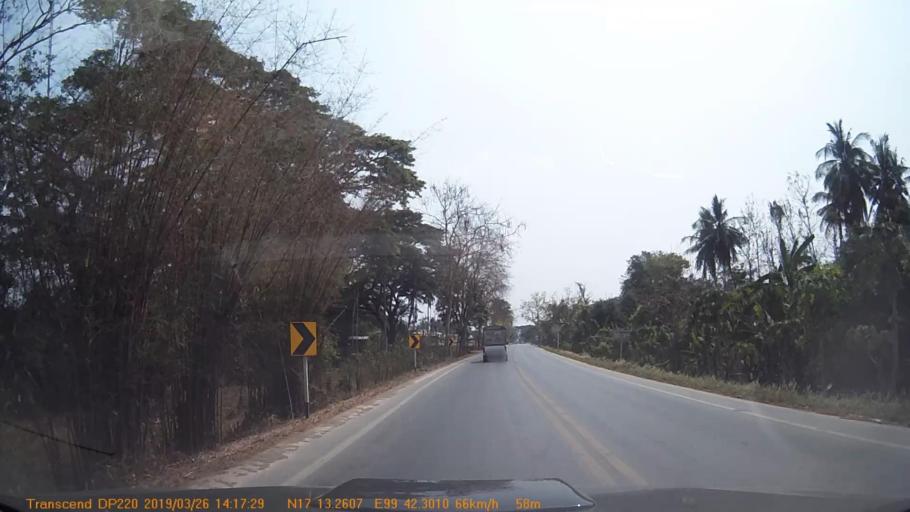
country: TH
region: Sukhothai
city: Sawankhalok
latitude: 17.2208
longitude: 99.7049
